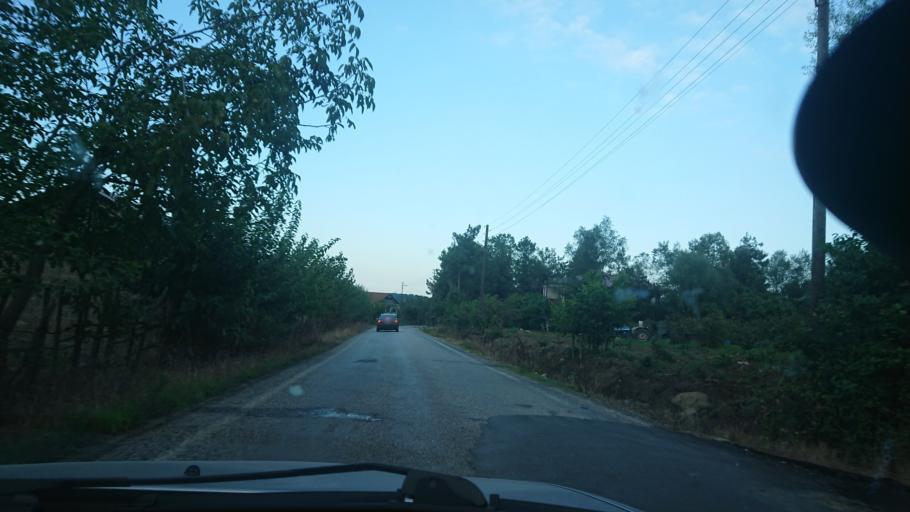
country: TR
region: Samsun
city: Tekkekoy
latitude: 41.1719
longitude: 36.5347
